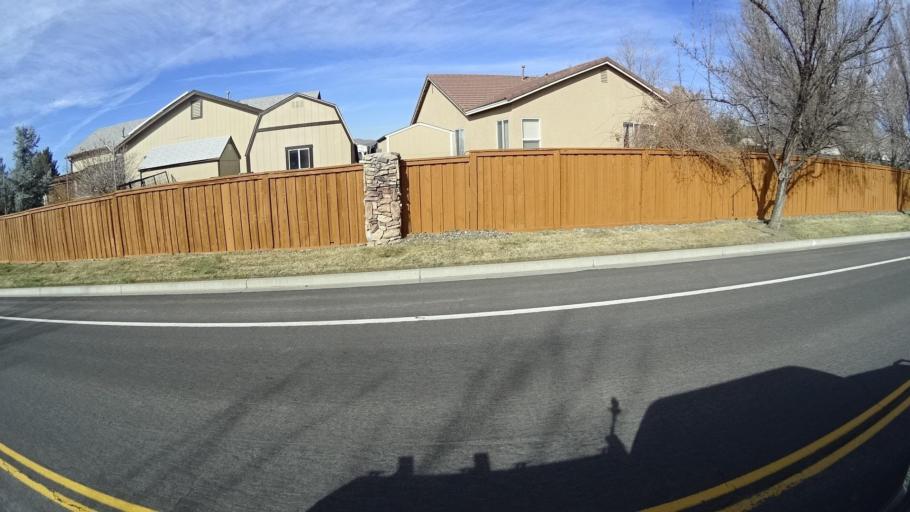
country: US
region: Nevada
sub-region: Washoe County
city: Spanish Springs
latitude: 39.6322
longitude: -119.6936
